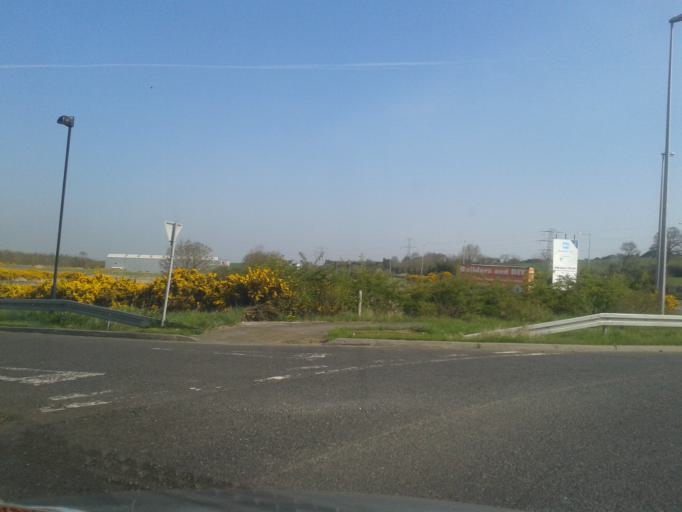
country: IE
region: Leinster
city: Balrothery
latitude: 53.5644
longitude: -6.2105
